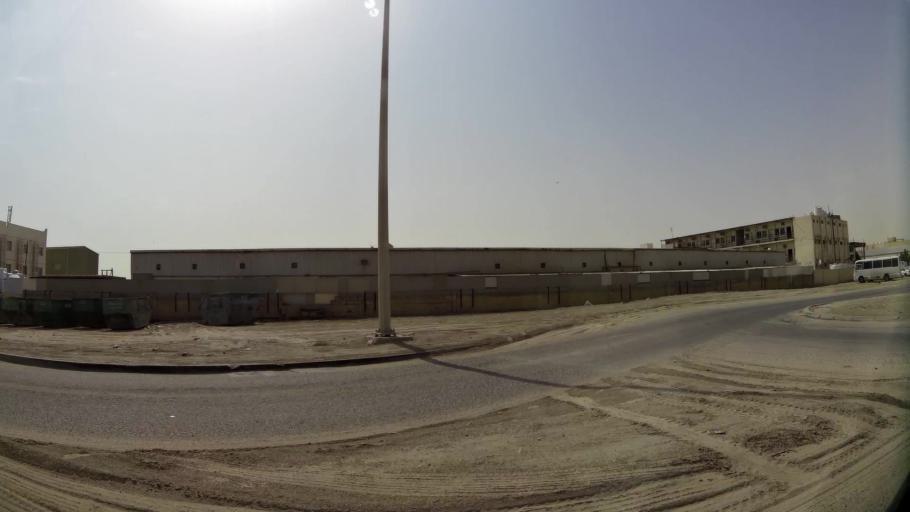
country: QA
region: Al Wakrah
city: Al Wukayr
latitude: 25.1713
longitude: 51.4668
